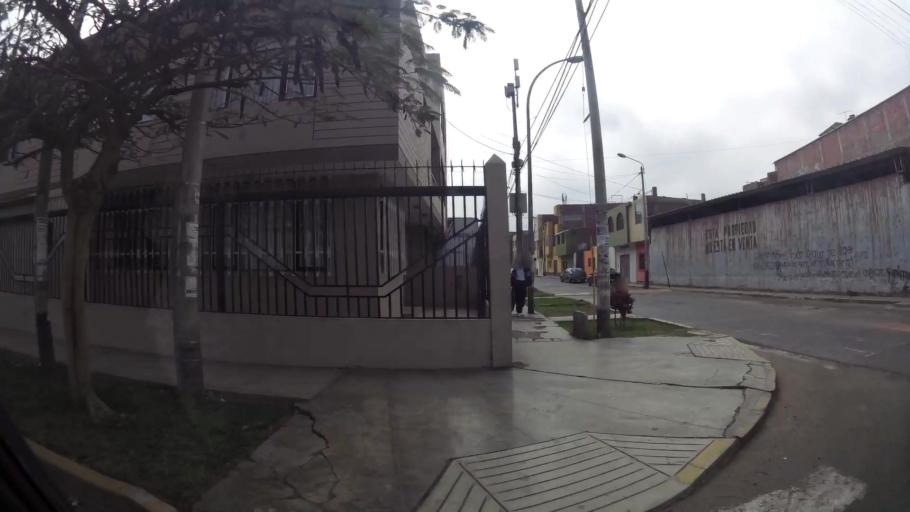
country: PE
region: La Libertad
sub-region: Provincia de Trujillo
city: Trujillo
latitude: -8.1173
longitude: -79.0224
